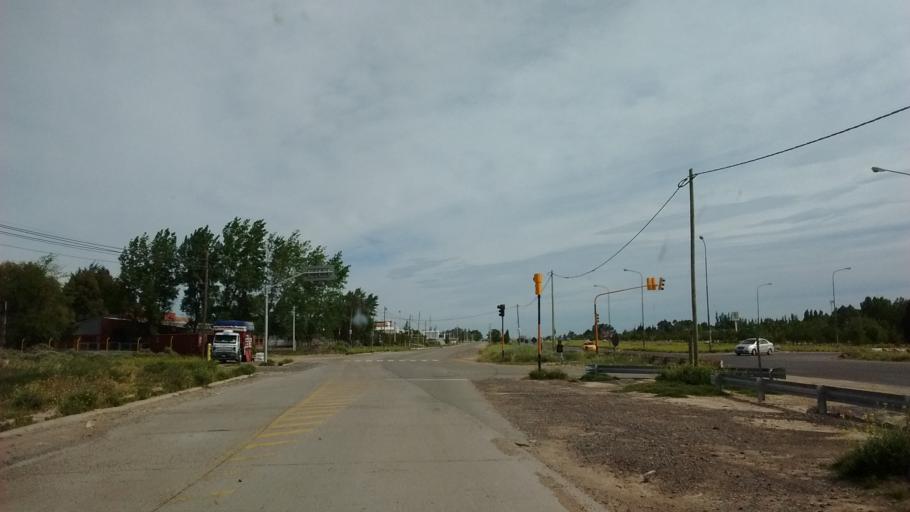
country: AR
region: Neuquen
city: Neuquen
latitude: -38.9080
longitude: -68.0829
